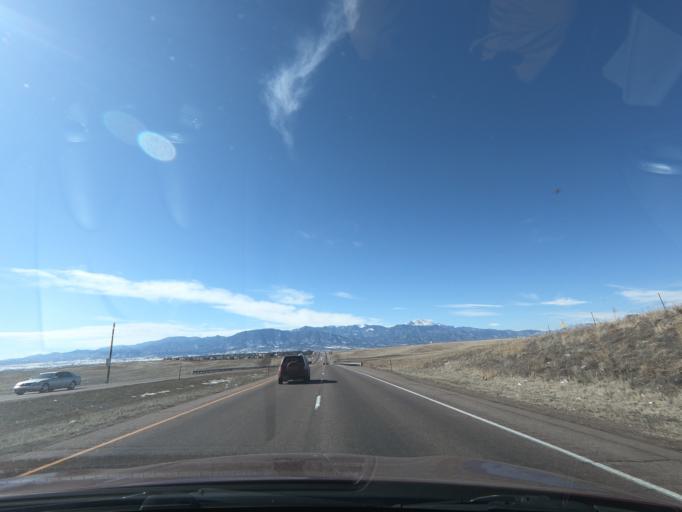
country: US
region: Colorado
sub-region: El Paso County
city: Security-Widefield
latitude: 38.7664
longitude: -104.6911
